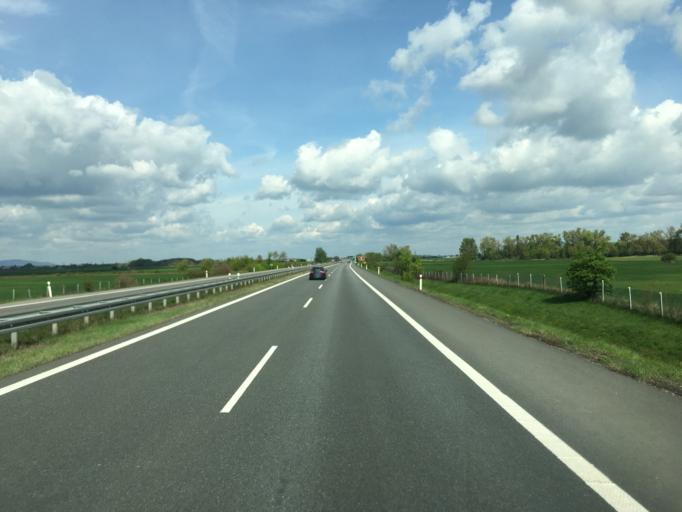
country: CZ
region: South Moravian
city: Kostice
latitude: 48.7656
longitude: 16.9425
